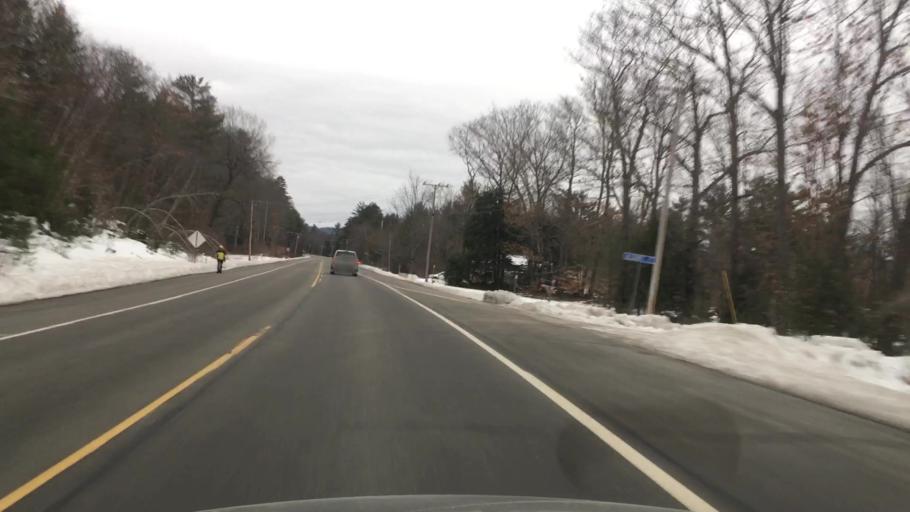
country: US
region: New Hampshire
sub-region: Merrimack County
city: Sutton
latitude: 43.2831
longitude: -71.9765
